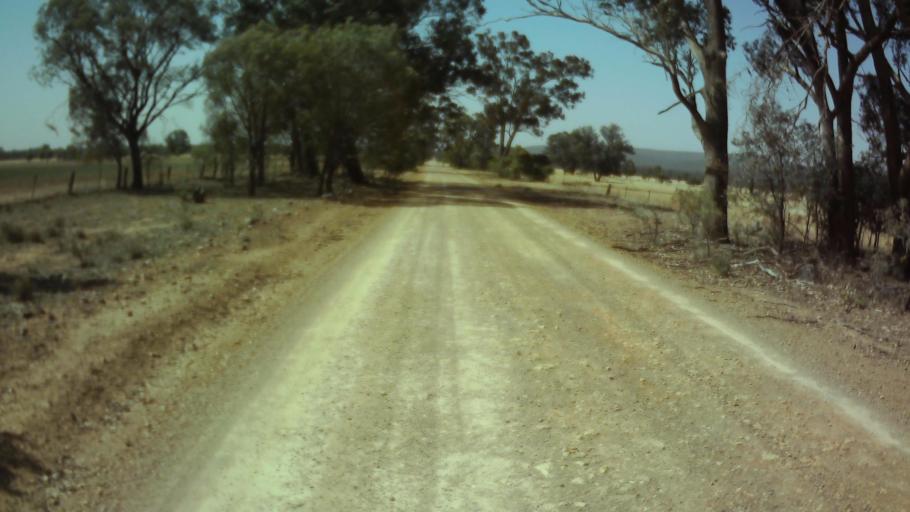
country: AU
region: New South Wales
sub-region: Weddin
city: Grenfell
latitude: -33.9895
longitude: 147.9267
